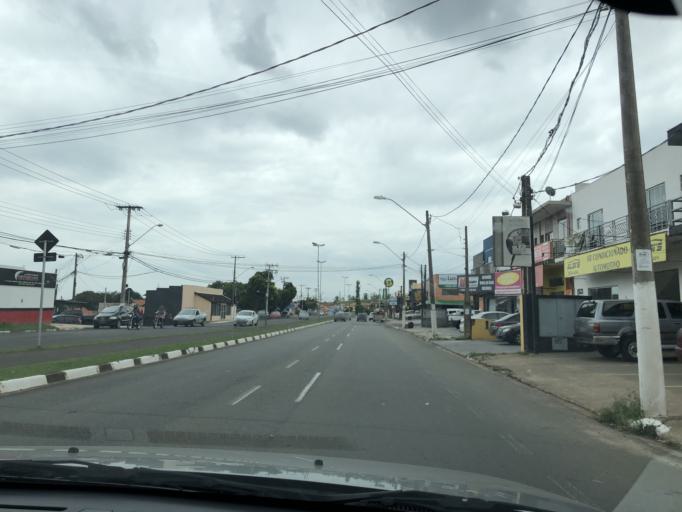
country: BR
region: Sao Paulo
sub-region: Paulinia
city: Paulinia
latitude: -22.7469
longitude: -47.1715
